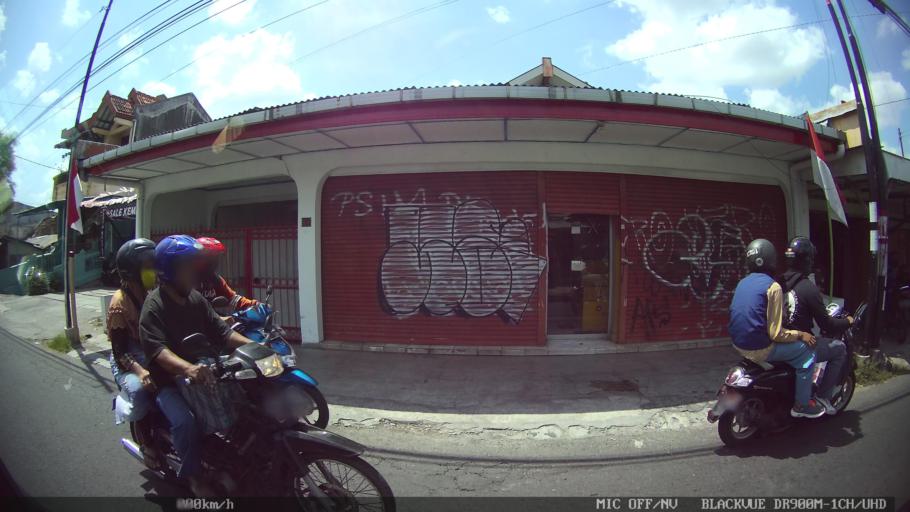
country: ID
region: Daerah Istimewa Yogyakarta
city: Kasihan
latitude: -7.8124
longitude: 110.3494
